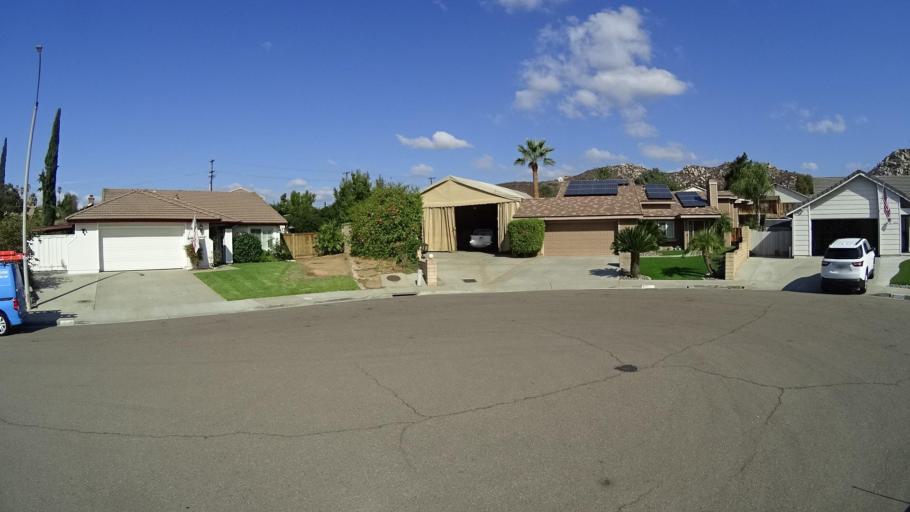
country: US
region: California
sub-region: San Diego County
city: Eucalyptus Hills
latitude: 32.8617
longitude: -116.9587
